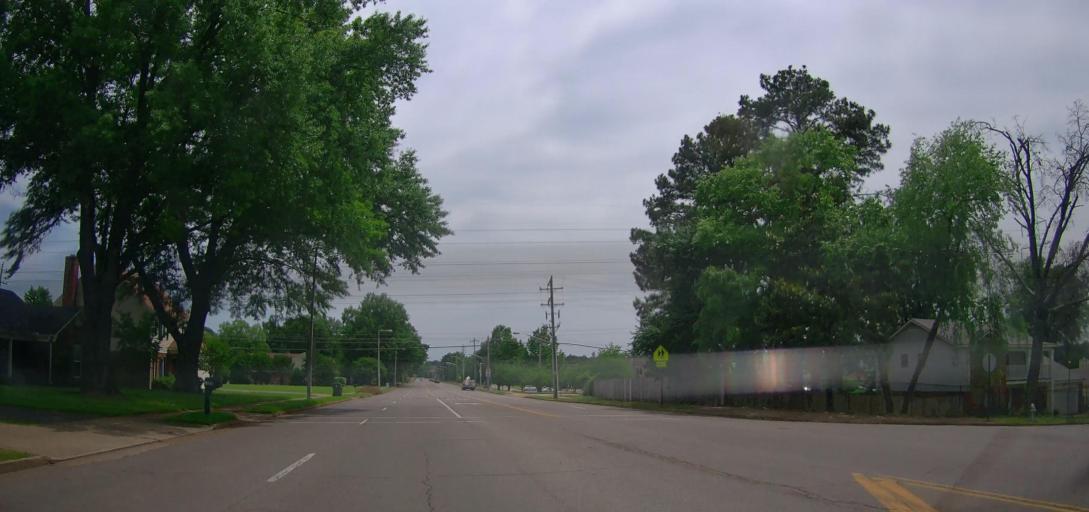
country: US
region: Tennessee
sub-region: Shelby County
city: Germantown
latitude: 35.0807
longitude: -89.8516
